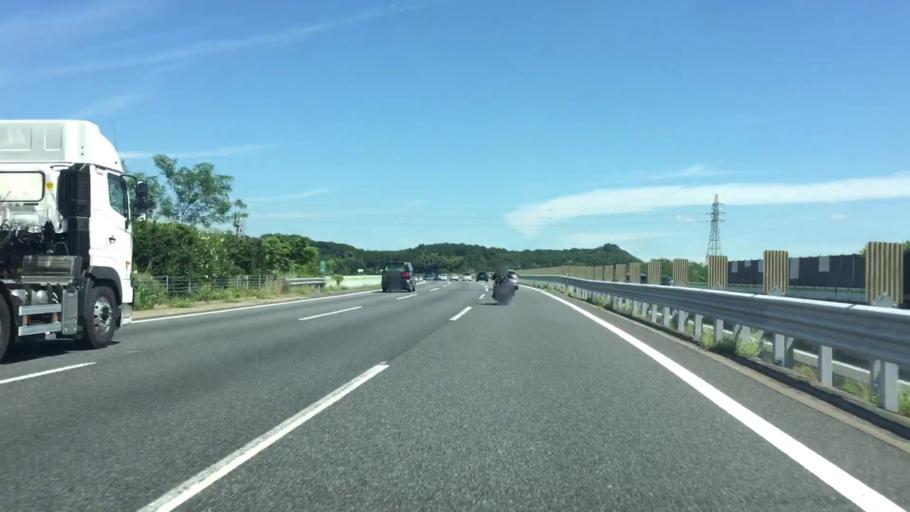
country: JP
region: Tochigi
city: Kanuma
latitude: 36.4789
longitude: 139.7457
